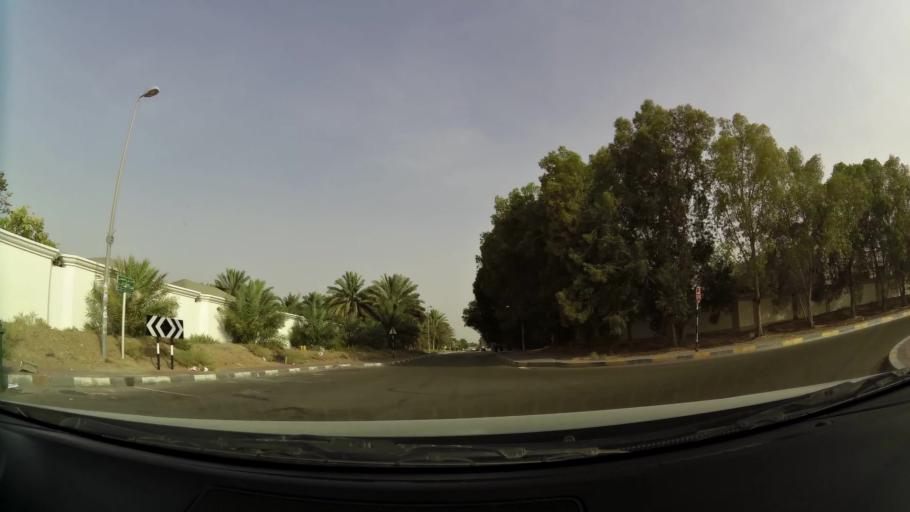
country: AE
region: Abu Dhabi
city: Al Ain
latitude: 24.2206
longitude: 55.6491
